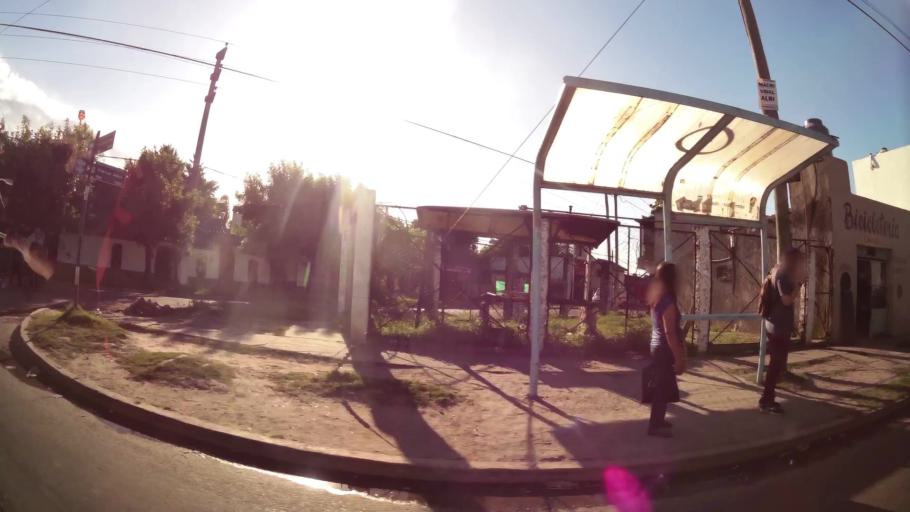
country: AR
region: Buenos Aires
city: Santa Catalina - Dique Lujan
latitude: -34.4958
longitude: -58.7284
